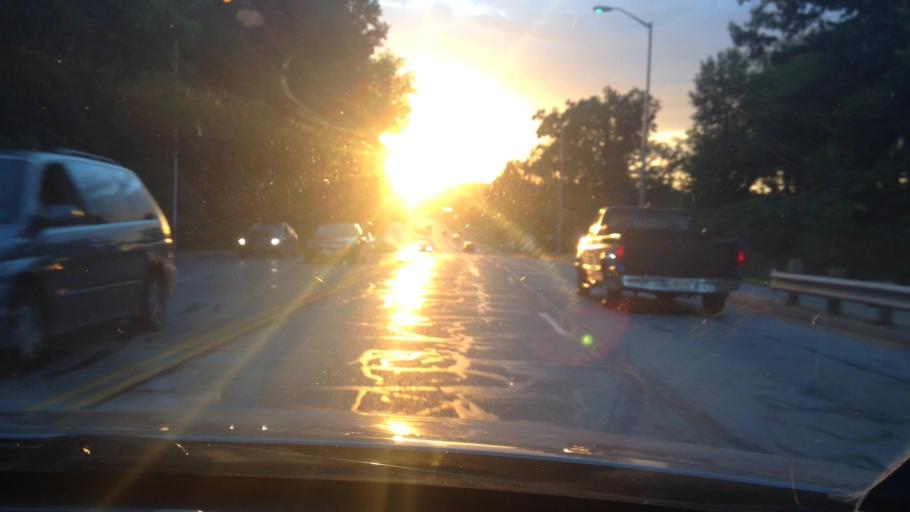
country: US
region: Missouri
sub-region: Jackson County
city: Raytown
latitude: 39.0346
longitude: -94.5283
